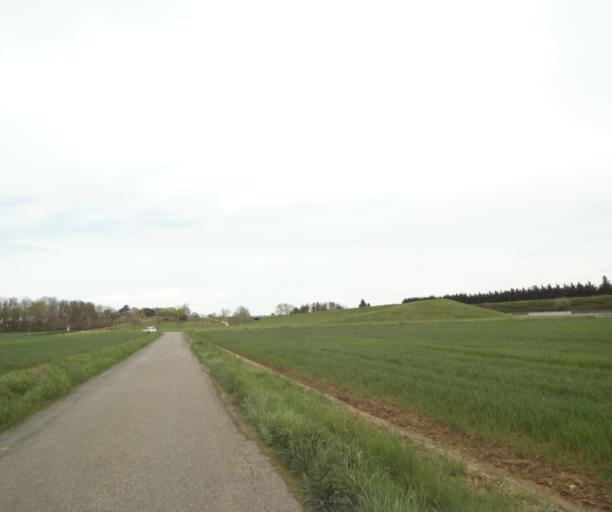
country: FR
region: Bourgogne
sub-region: Departement de Saone-et-Loire
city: Charnay-les-Macon
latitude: 46.3067
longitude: 4.7926
